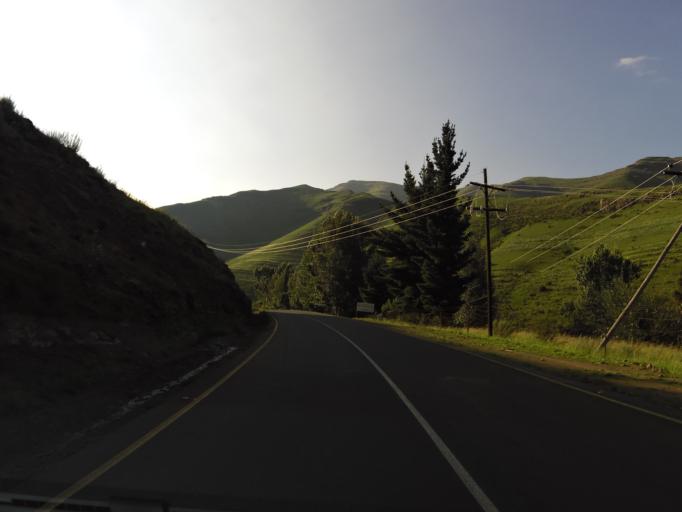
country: LS
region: Butha-Buthe
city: Butha-Buthe
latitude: -29.1108
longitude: 28.4696
